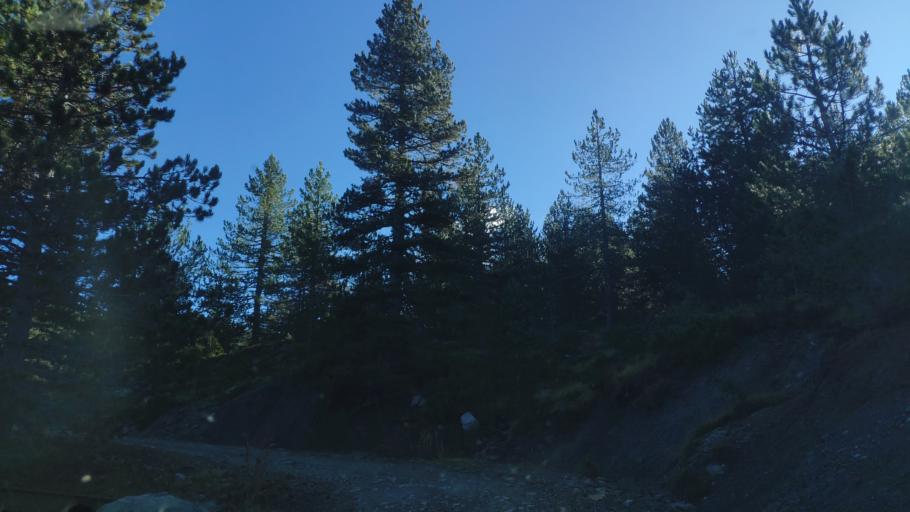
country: GR
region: Epirus
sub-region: Nomos Ioanninon
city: Metsovo
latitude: 39.8342
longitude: 21.1327
